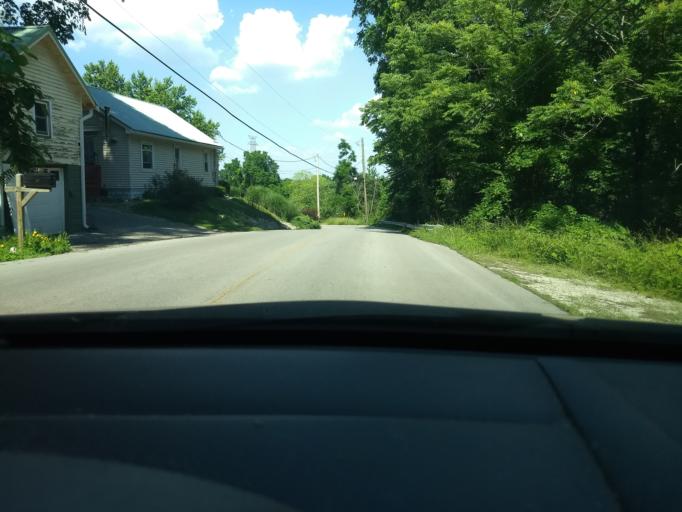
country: US
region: Indiana
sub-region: Floyd County
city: New Albany
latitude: 38.2659
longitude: -85.8553
